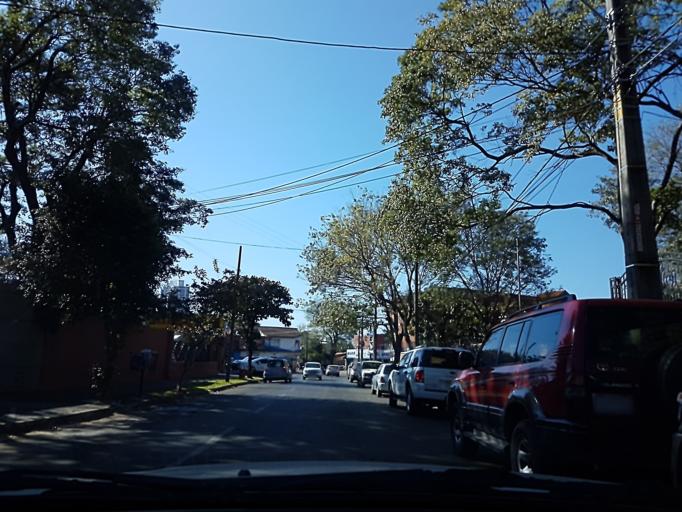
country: PY
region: Central
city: Fernando de la Mora
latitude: -25.2936
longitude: -57.5590
